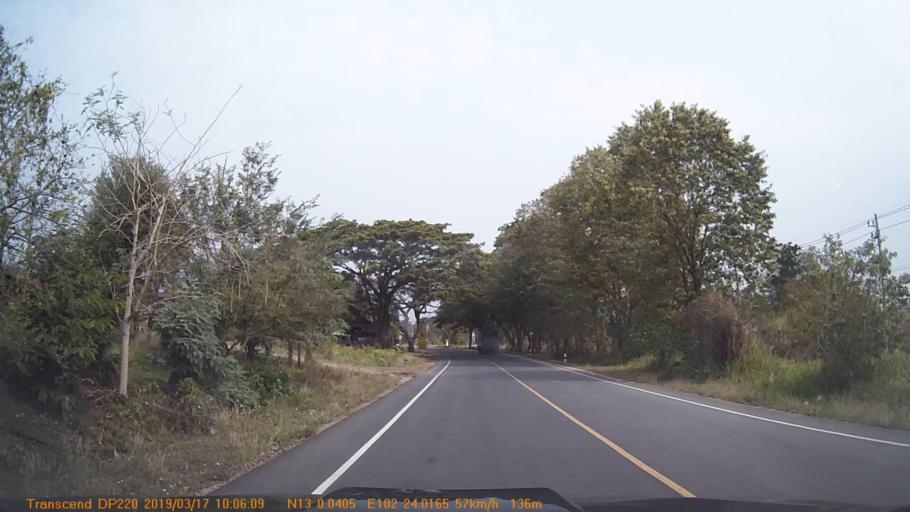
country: TH
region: Chanthaburi
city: Pong Nam Ron
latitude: 13.0023
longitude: 102.3999
